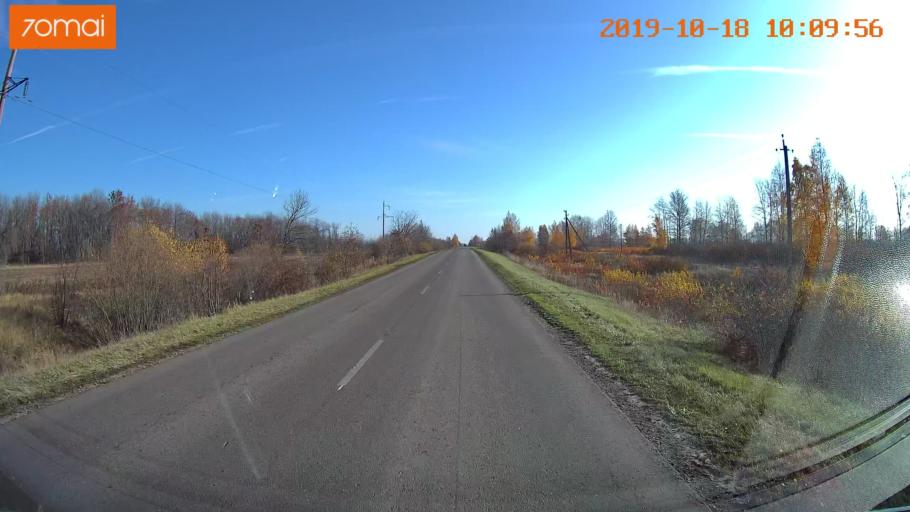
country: RU
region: Tula
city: Kurkino
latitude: 53.3780
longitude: 38.4670
